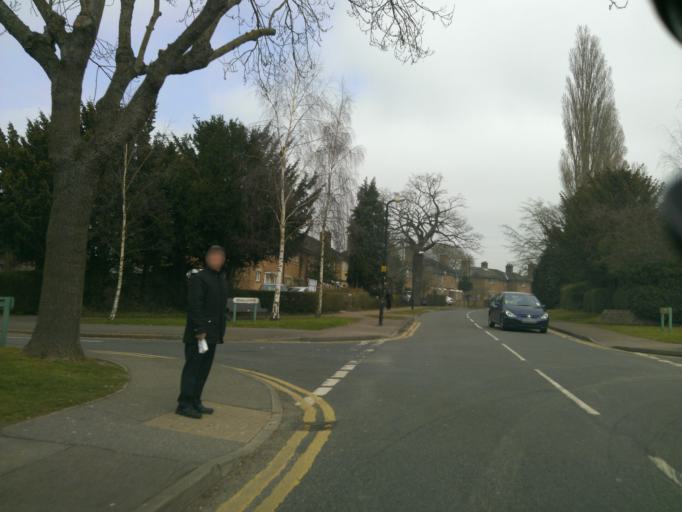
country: GB
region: England
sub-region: Essex
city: Rayne
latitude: 51.8455
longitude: 0.6228
